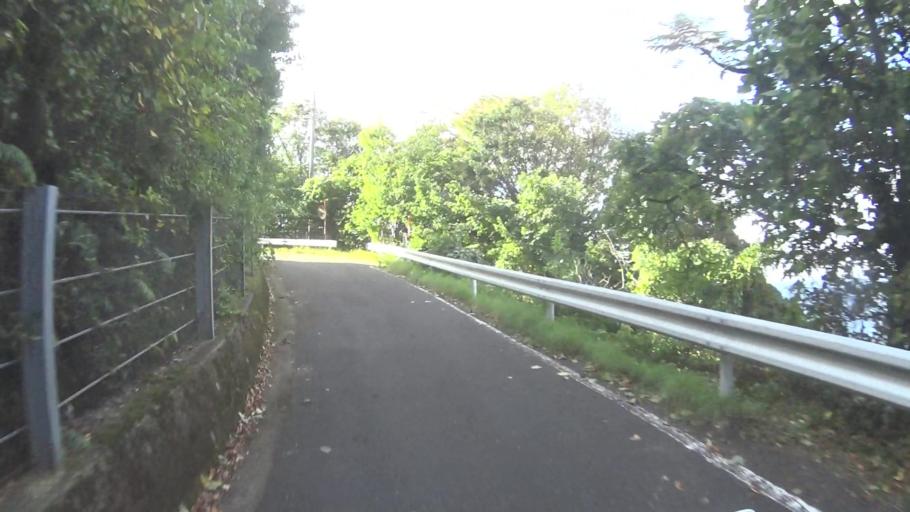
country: JP
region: Kyoto
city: Maizuru
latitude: 35.5686
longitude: 135.4135
